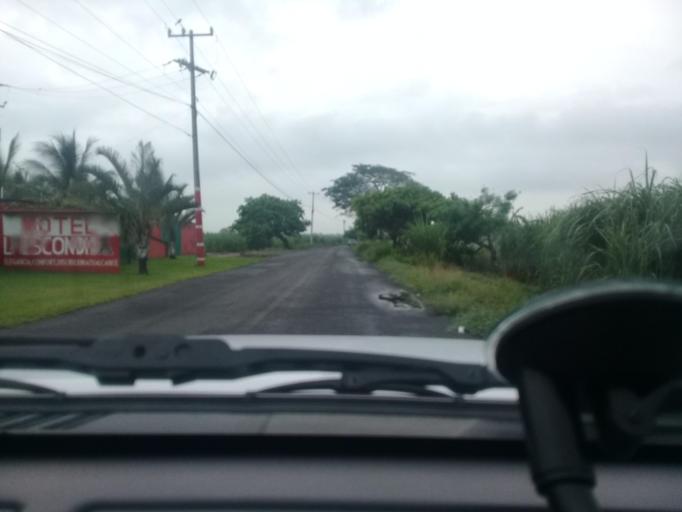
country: MX
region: Veracruz
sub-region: La Antigua
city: Nicolas Blanco (San Pancho)
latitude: 19.3533
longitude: -96.3472
